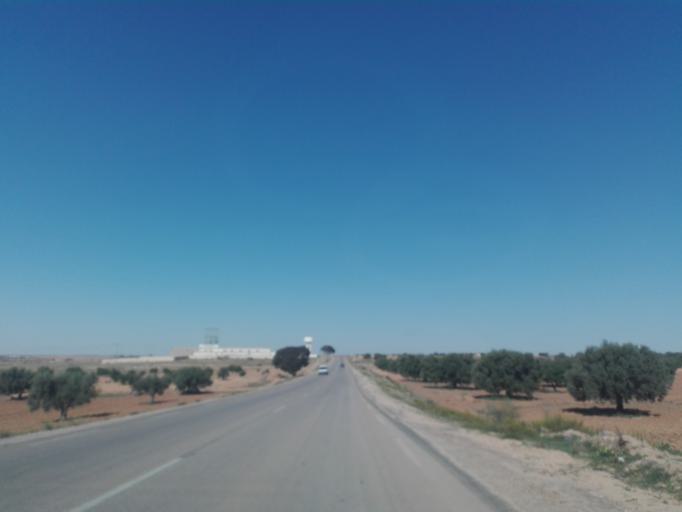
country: TN
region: Safaqis
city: Bi'r `Ali Bin Khalifah
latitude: 34.7393
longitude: 10.3994
